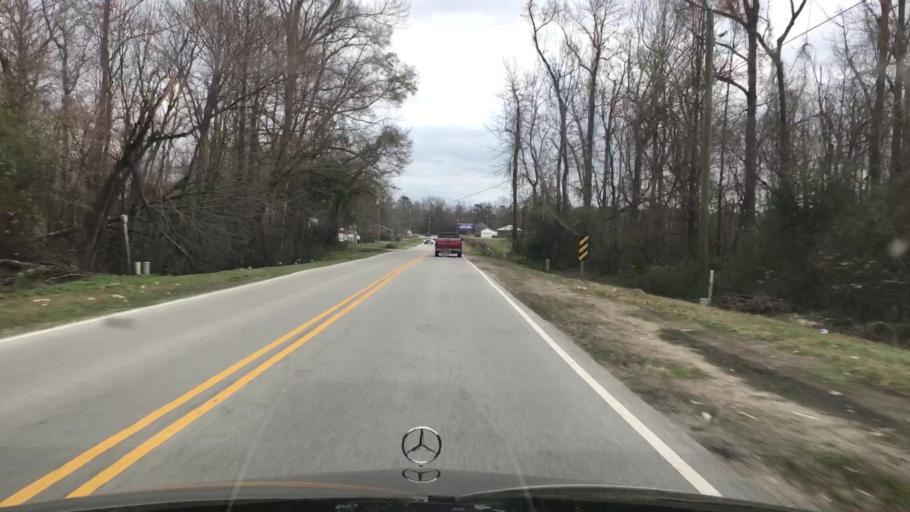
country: US
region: North Carolina
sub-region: Onslow County
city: Richlands
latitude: 34.8797
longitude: -77.5205
